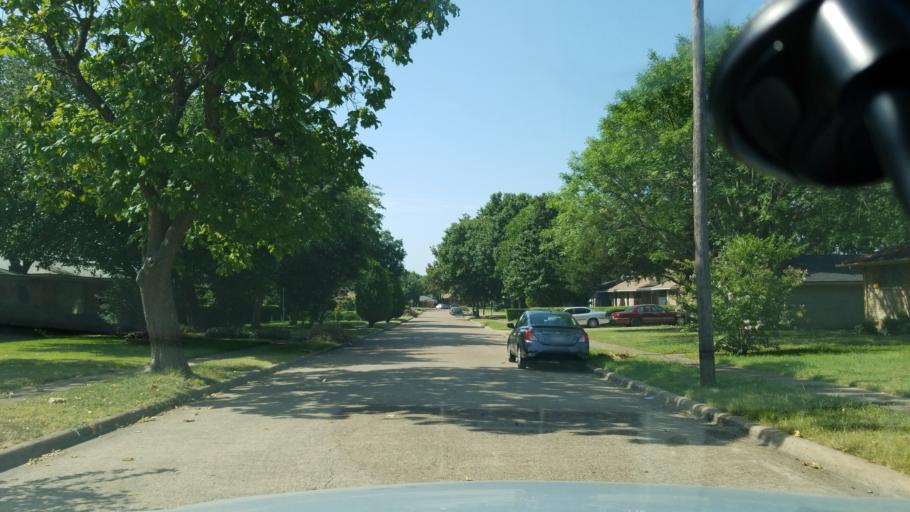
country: US
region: Texas
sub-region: Dallas County
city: Duncanville
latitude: 32.6812
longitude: -96.8491
